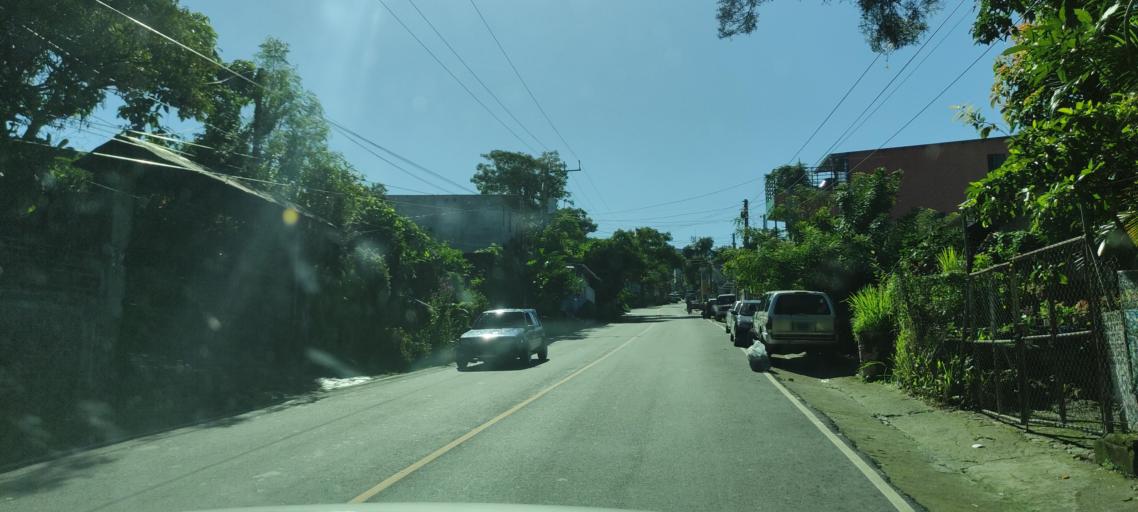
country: HN
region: Ocotepeque
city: Antigua Ocotepeque
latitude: 14.3188
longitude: -89.1731
